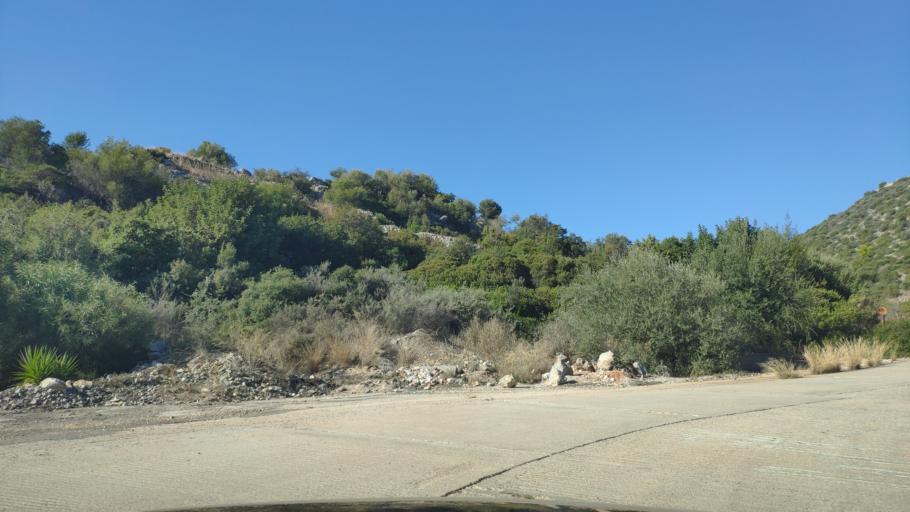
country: GR
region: Attica
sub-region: Nomos Piraios
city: Galatas
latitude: 37.5595
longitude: 23.3645
